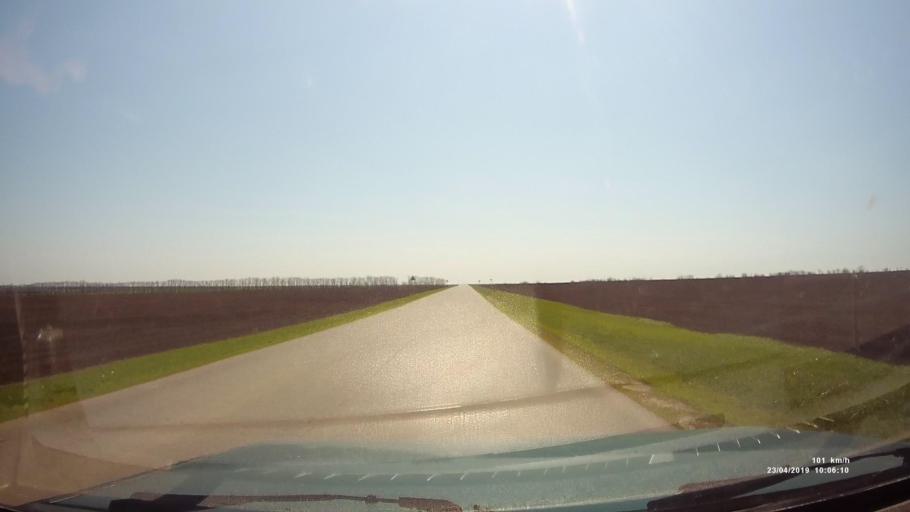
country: RU
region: Rostov
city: Sovetskoye
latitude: 46.7354
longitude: 42.2318
